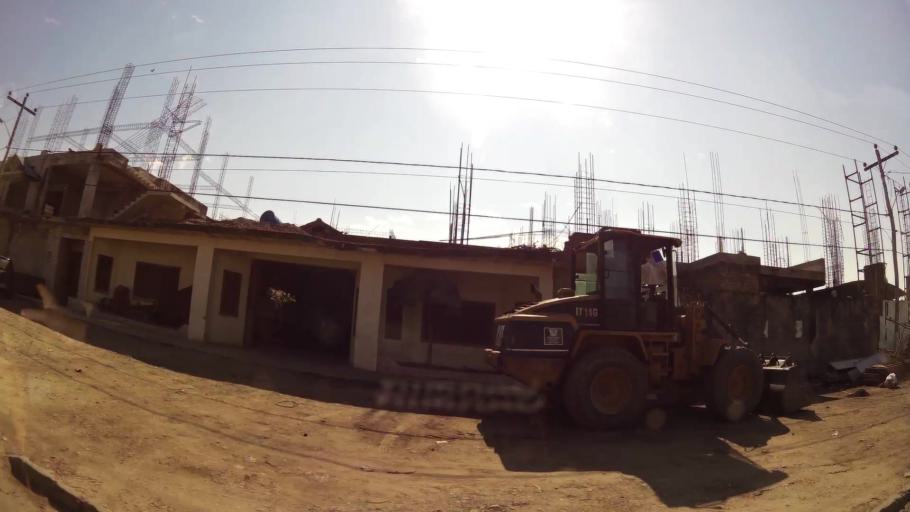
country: BO
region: Santa Cruz
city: Santa Cruz de la Sierra
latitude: -17.7615
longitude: -63.1105
